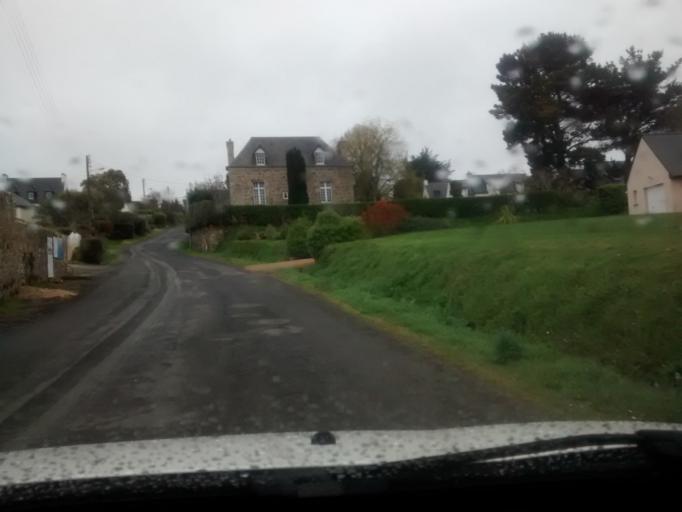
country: FR
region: Brittany
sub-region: Departement des Cotes-d'Armor
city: Penvenan
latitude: 48.8359
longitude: -3.2819
